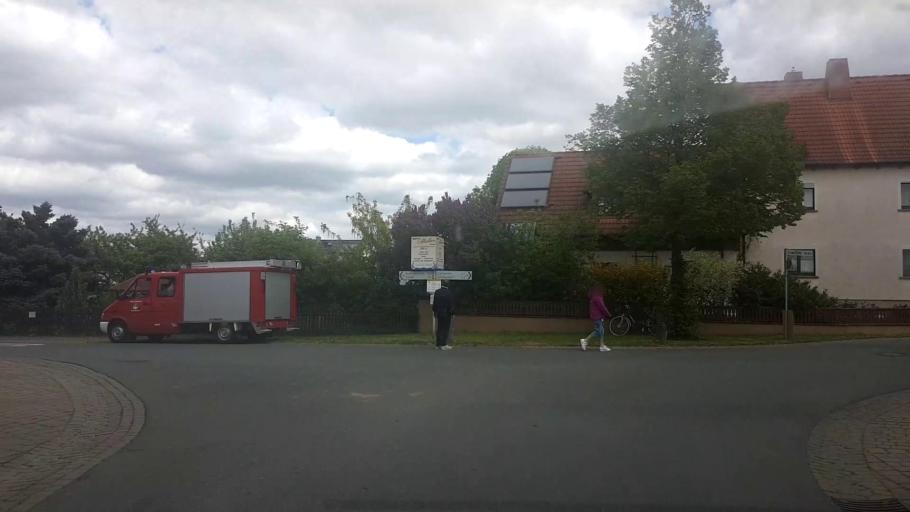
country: DE
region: Bavaria
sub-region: Upper Franconia
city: Lichtenfels
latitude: 50.1318
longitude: 11.0264
